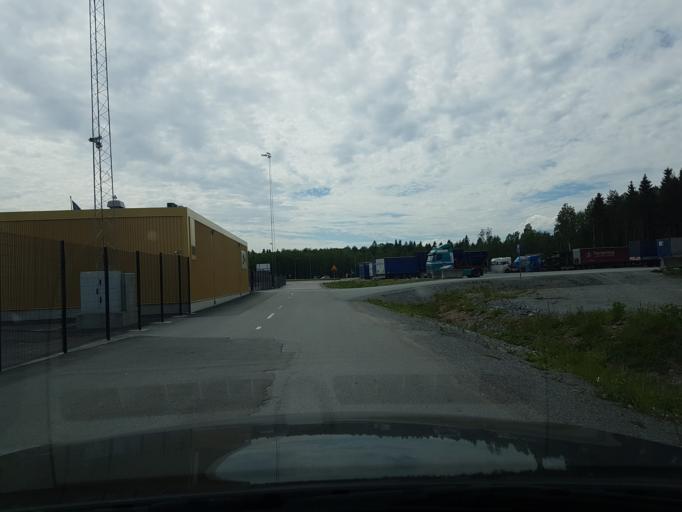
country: SE
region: Stockholm
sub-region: Norrtalje Kommun
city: Bjorko
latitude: 59.7230
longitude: 19.0615
